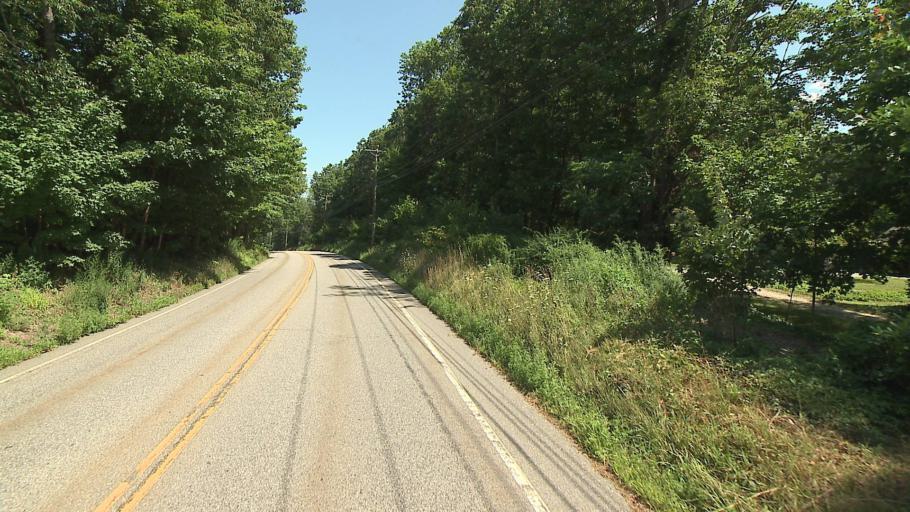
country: US
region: Connecticut
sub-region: Litchfield County
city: Northwest Harwinton
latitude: 41.7768
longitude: -72.9980
